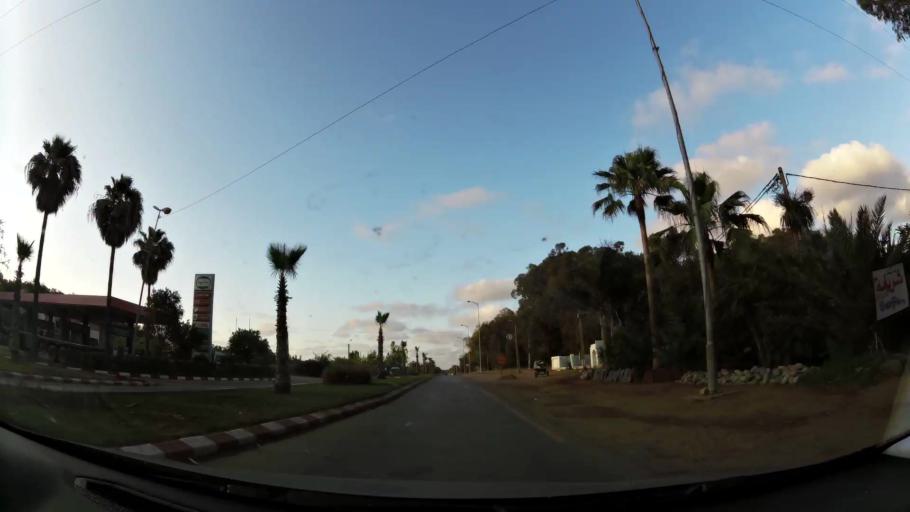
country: MA
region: Gharb-Chrarda-Beni Hssen
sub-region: Kenitra Province
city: Kenitra
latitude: 34.2036
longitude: -6.6760
